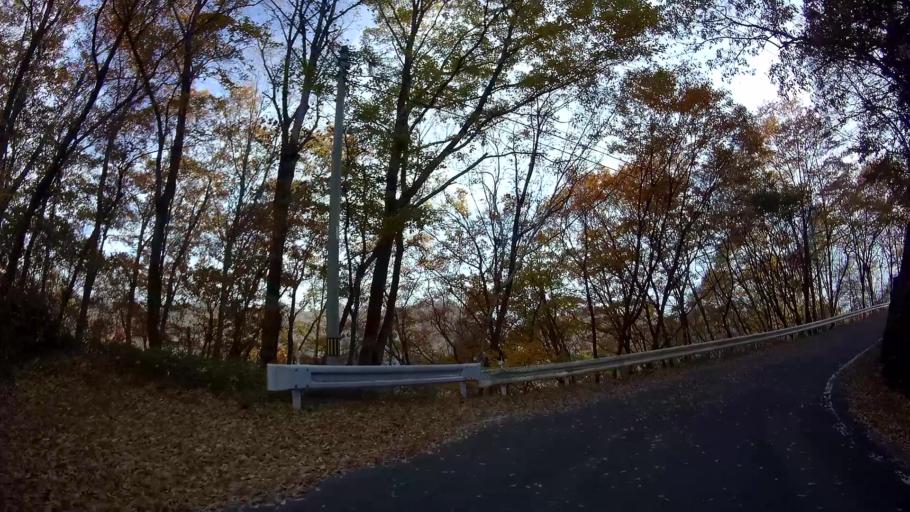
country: JP
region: Gunma
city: Nakanojomachi
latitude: 36.6206
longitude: 138.6365
